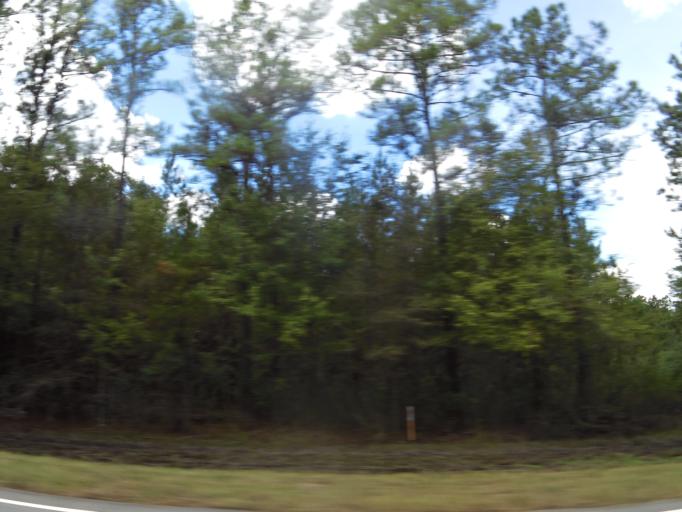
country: US
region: Georgia
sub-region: Brantley County
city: Nahunta
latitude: 31.0636
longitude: -82.0142
